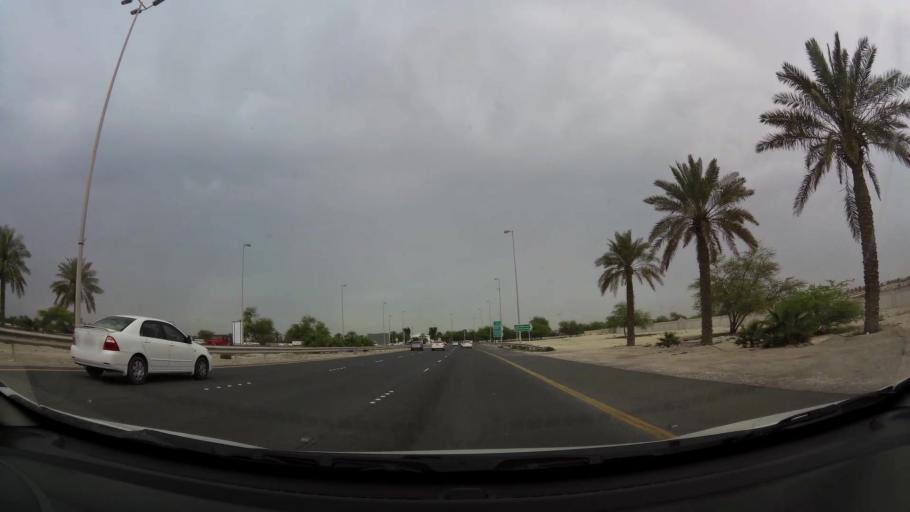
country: BH
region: Central Governorate
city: Dar Kulayb
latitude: 26.0547
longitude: 50.4999
